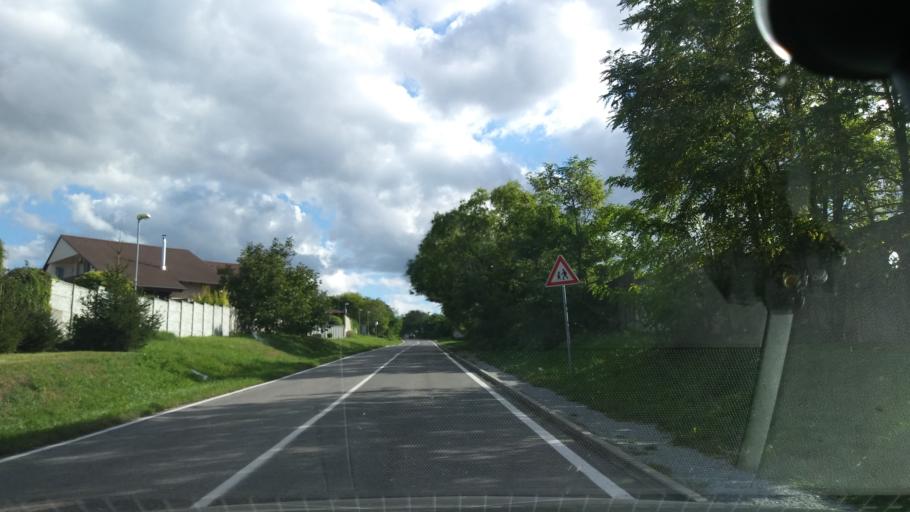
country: SK
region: Trnavsky
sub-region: Okres Skalica
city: Holic
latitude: 48.7996
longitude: 17.1642
